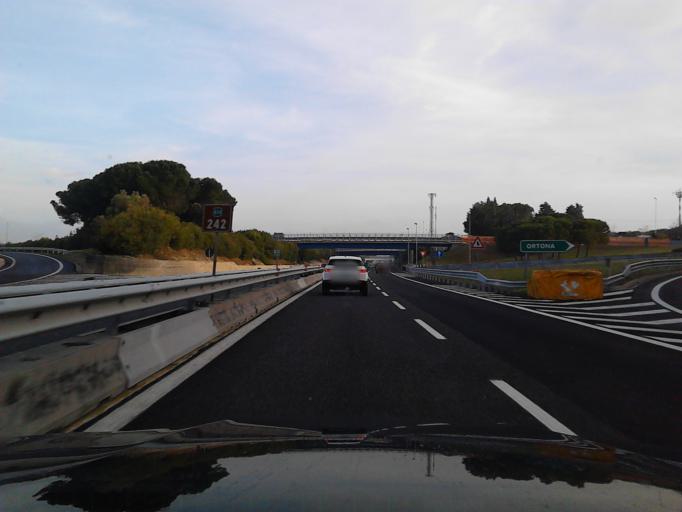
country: IT
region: Abruzzo
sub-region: Provincia di Chieti
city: Ortona
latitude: 42.3307
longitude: 14.3805
